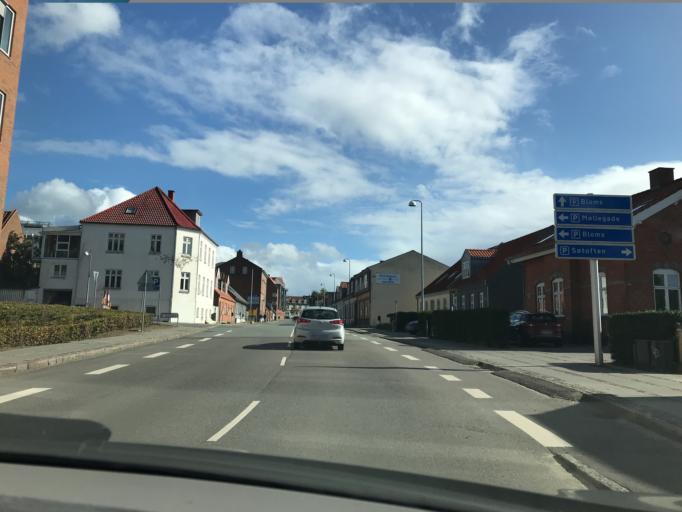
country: DK
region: Central Jutland
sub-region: Skanderborg Kommune
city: Skanderborg
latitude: 56.0327
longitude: 9.9280
